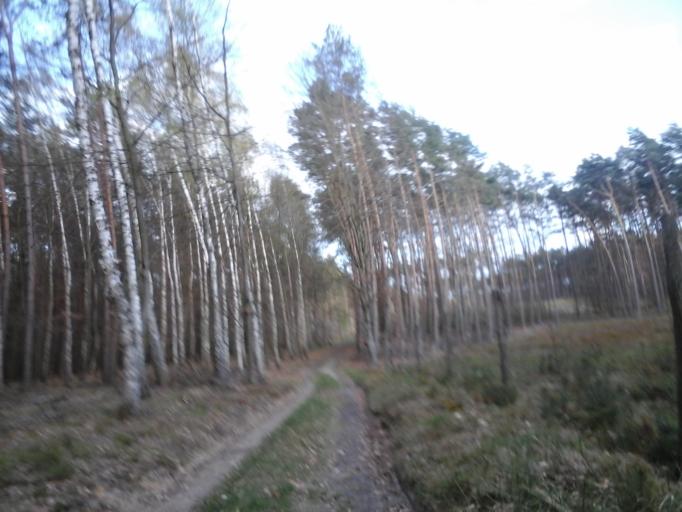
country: PL
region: West Pomeranian Voivodeship
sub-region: Powiat choszczenski
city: Bierzwnik
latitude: 53.0175
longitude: 15.6029
